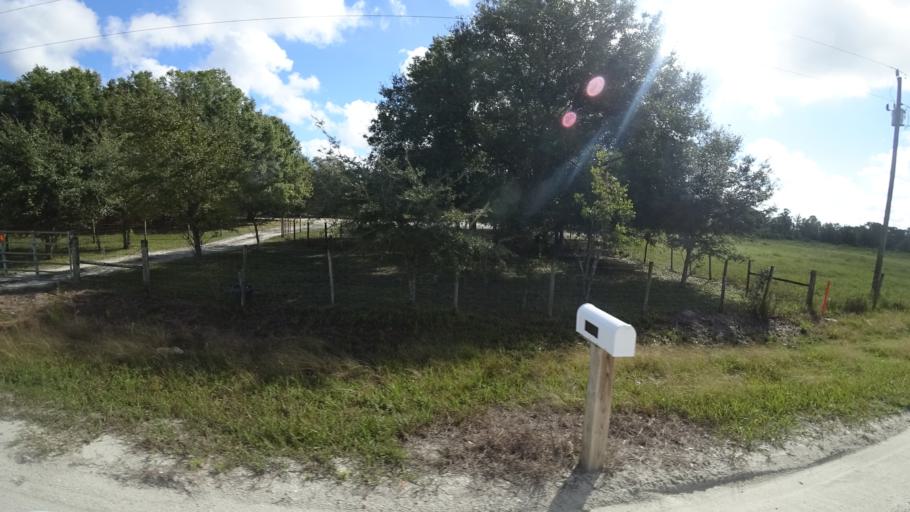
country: US
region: Florida
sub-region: Sarasota County
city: Lake Sarasota
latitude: 27.3301
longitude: -82.2041
